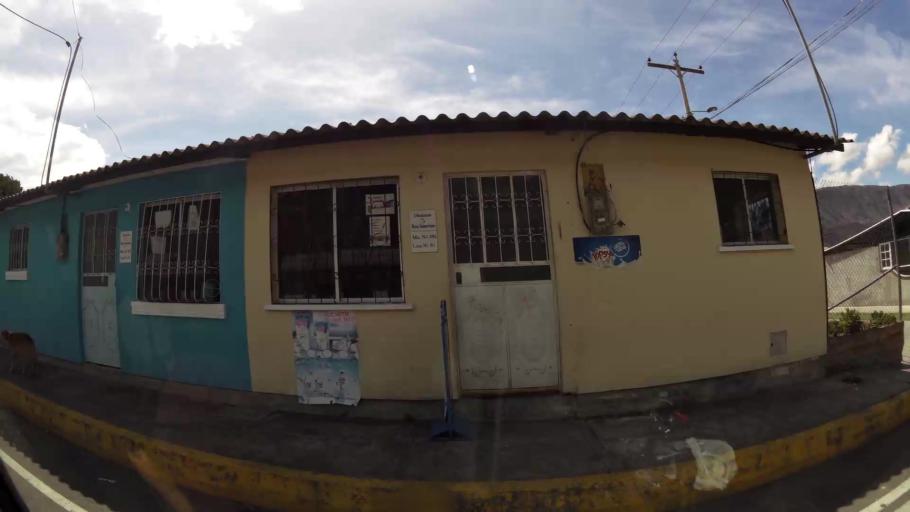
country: EC
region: Chimborazo
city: Guano
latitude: -1.5688
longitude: -78.5324
